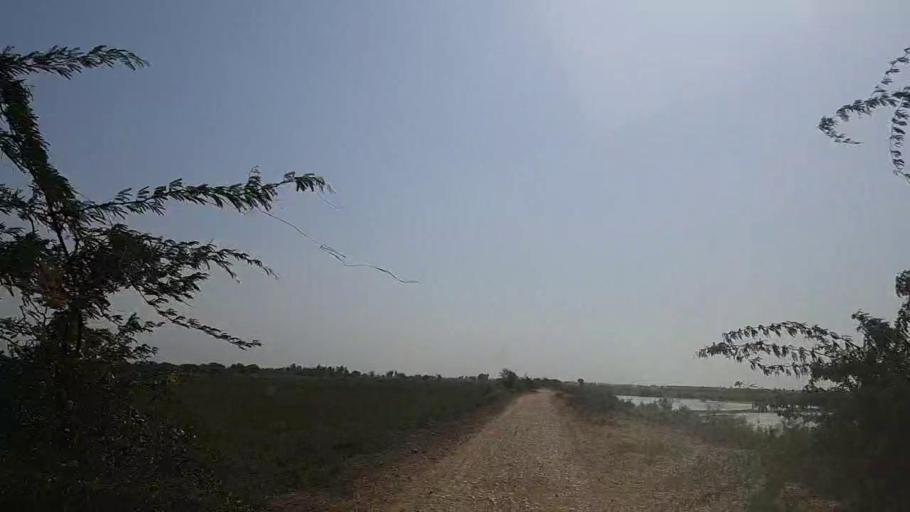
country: PK
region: Sindh
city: Daro Mehar
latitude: 24.7145
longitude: 68.1198
